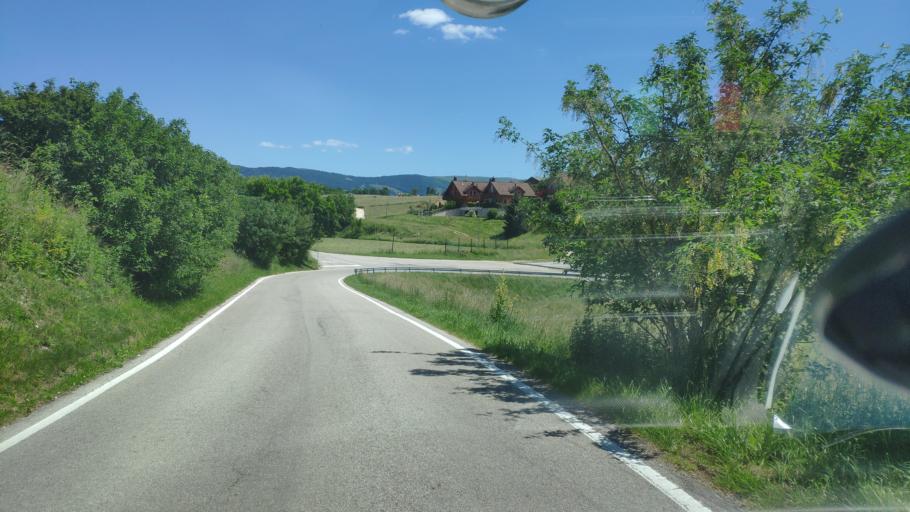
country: IT
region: Veneto
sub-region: Provincia di Vicenza
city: Canove di Roana
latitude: 45.8638
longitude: 11.4763
